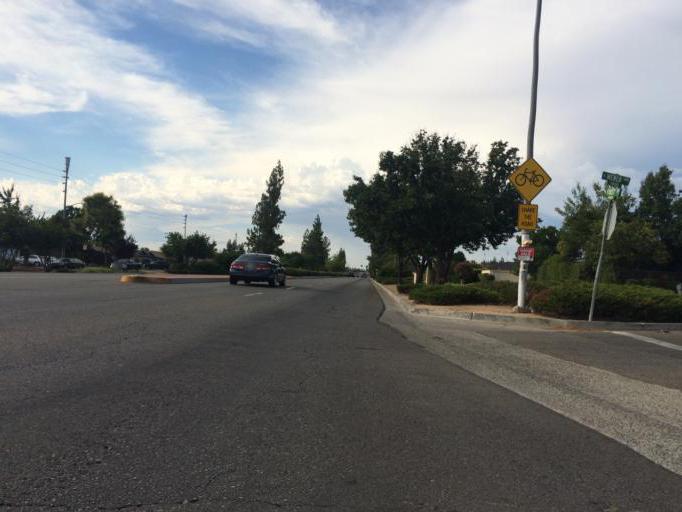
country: US
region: California
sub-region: Fresno County
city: Clovis
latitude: 36.8309
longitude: -119.7722
